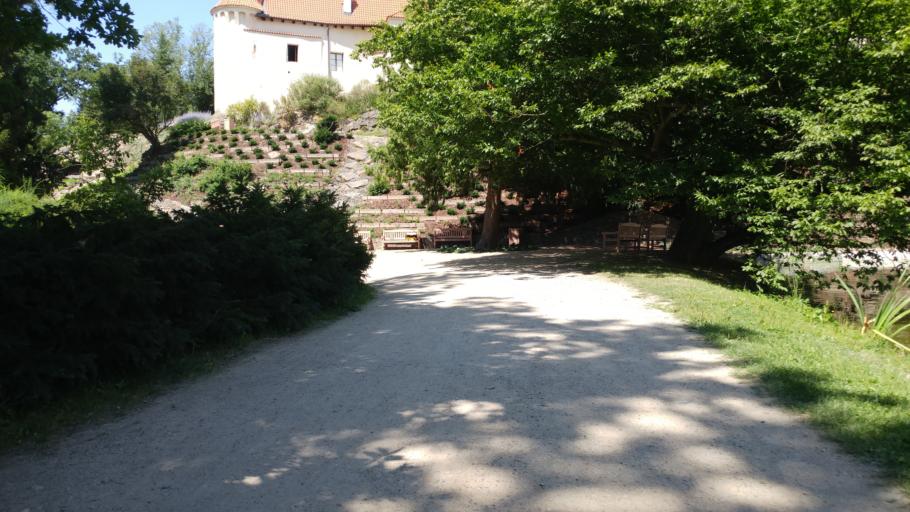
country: CZ
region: Central Bohemia
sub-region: Okres Praha-Zapad
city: Pruhonice
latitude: 49.9998
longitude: 14.5574
